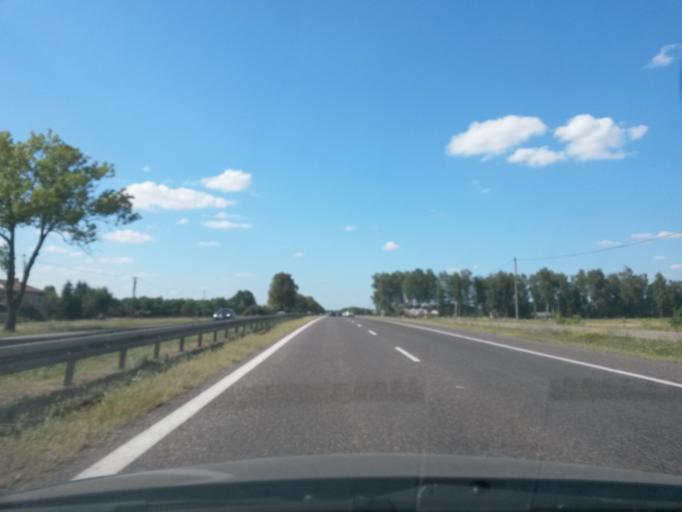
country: PL
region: Masovian Voivodeship
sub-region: Powiat plonski
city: Zaluski
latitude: 52.5384
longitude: 20.5120
